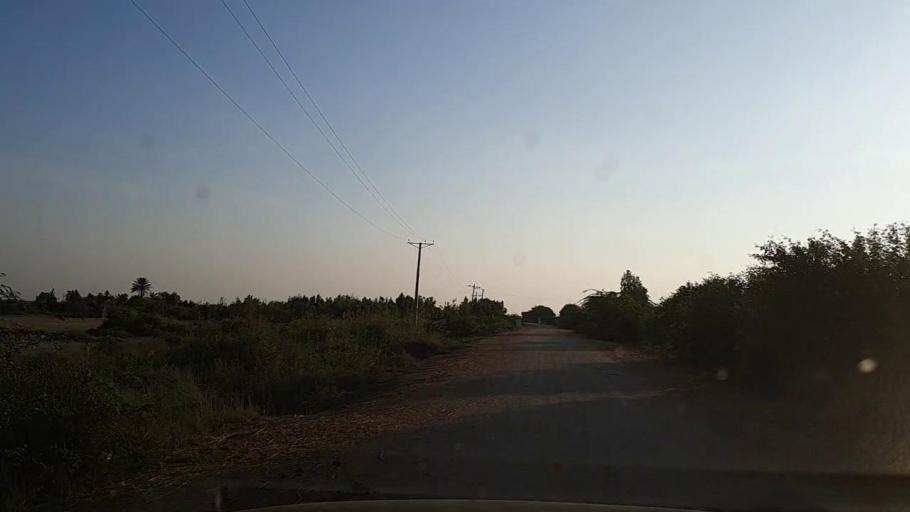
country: PK
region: Sindh
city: Thatta
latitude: 24.6247
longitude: 67.9148
